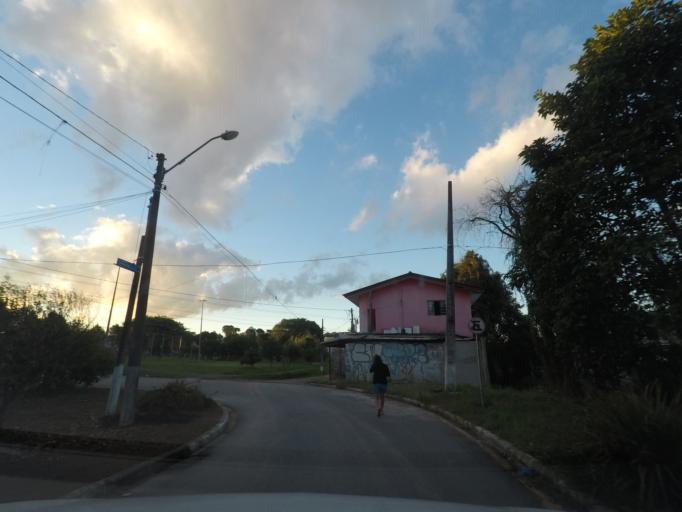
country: BR
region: Parana
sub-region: Sao Jose Dos Pinhais
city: Sao Jose dos Pinhais
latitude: -25.4994
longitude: -49.2590
